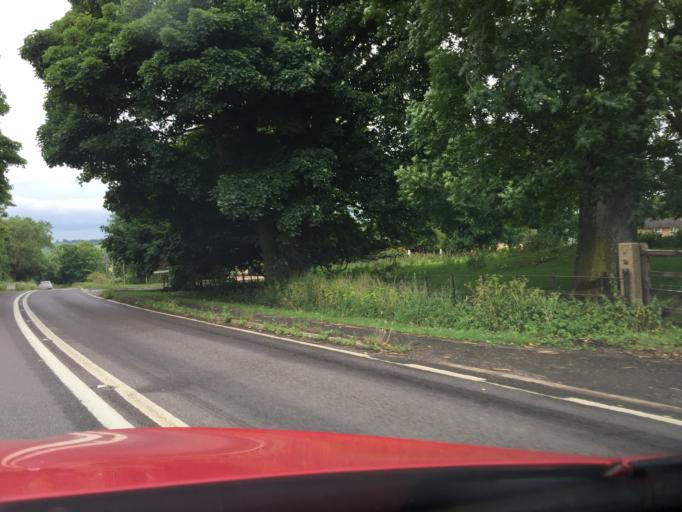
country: GB
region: England
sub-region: Northamptonshire
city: Daventry
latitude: 52.2459
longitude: -1.2157
